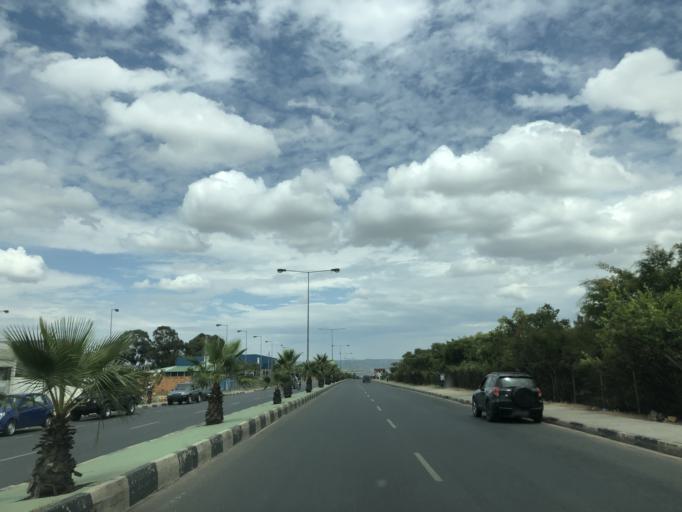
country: AO
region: Huila
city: Lubango
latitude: -14.9274
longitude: 13.5594
